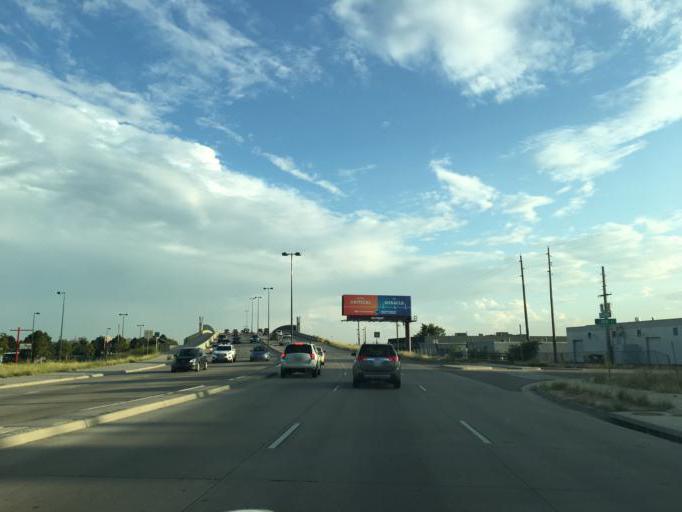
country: US
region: Colorado
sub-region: Adams County
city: Aurora
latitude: 39.7700
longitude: -104.8474
